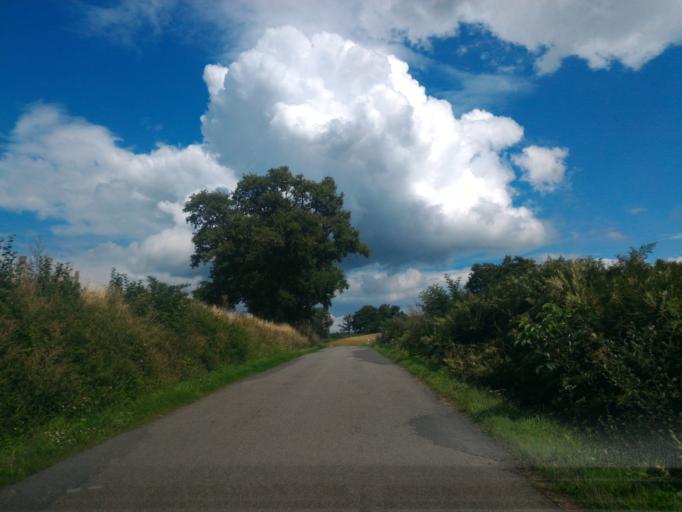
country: FR
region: Poitou-Charentes
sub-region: Departement de la Charente
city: Brigueuil
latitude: 45.9552
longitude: 0.8336
